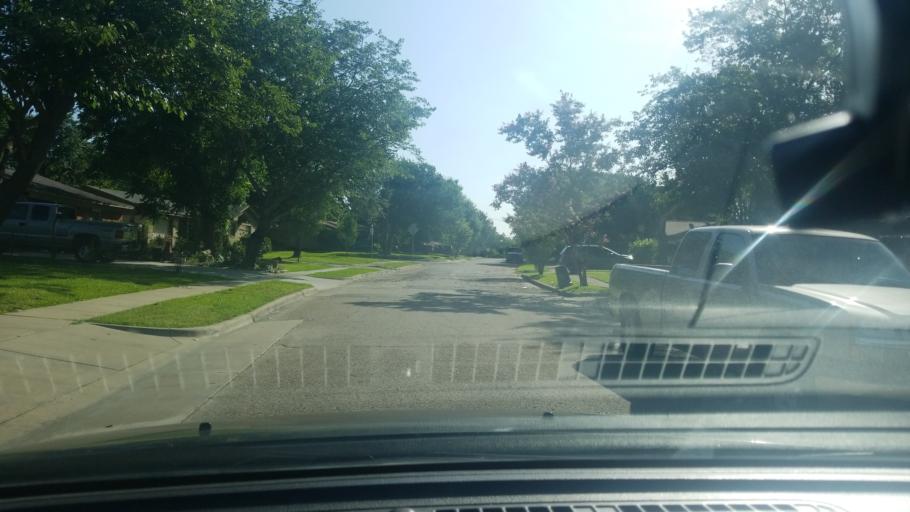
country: US
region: Texas
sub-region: Dallas County
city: Mesquite
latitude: 32.8119
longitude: -96.6547
